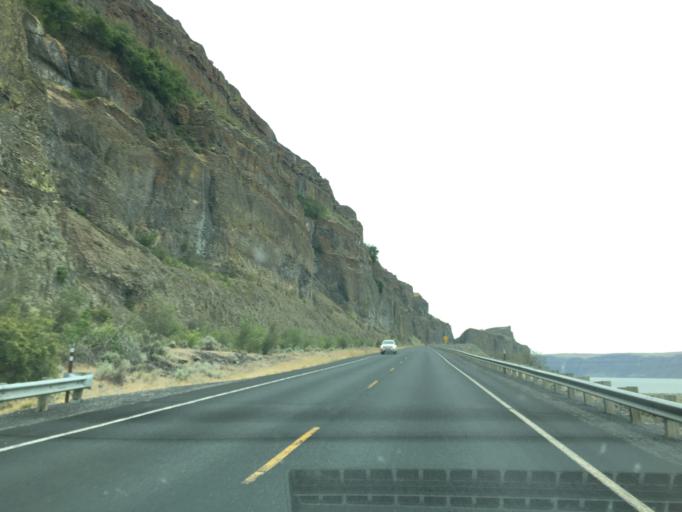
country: US
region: Washington
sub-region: Okanogan County
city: Coulee Dam
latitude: 47.7495
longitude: -119.2238
